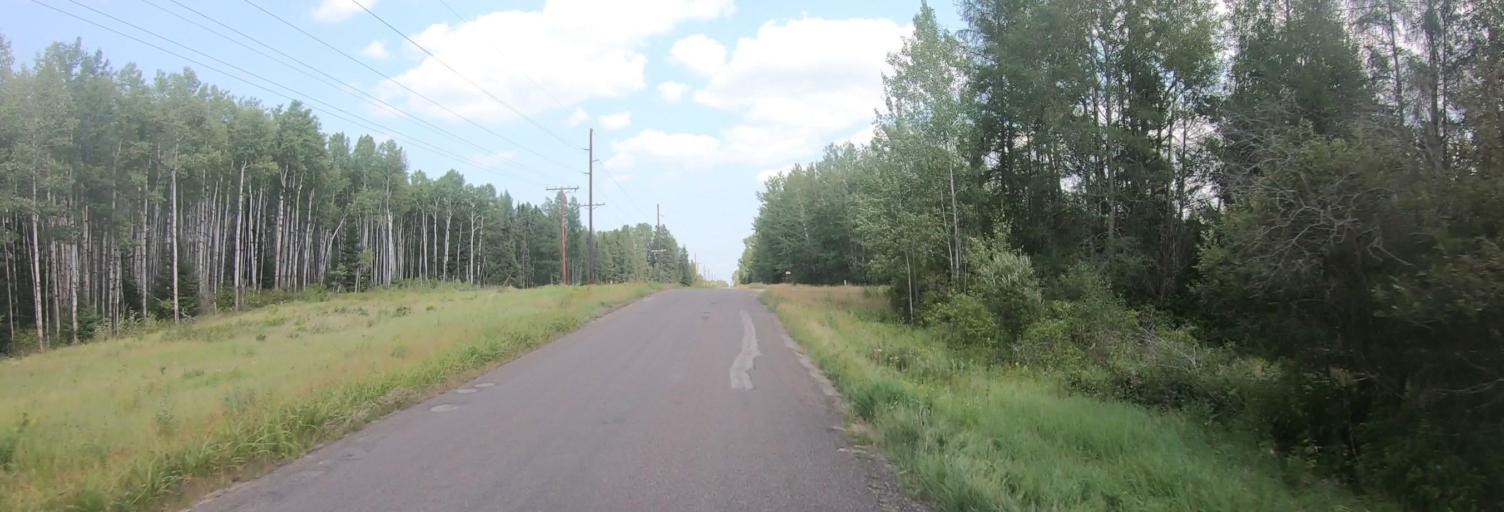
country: US
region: Minnesota
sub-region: Saint Louis County
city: Mountain Iron
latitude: 47.8920
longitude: -92.7341
